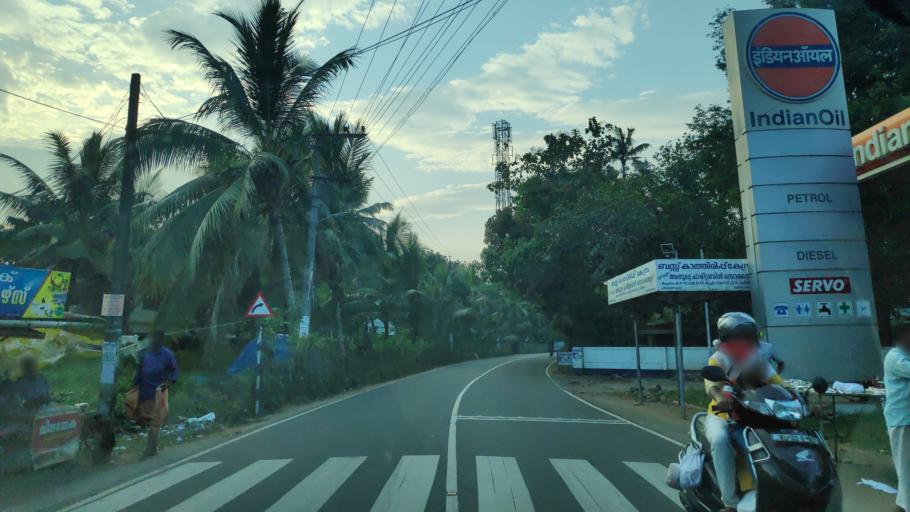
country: IN
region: Kerala
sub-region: Alappuzha
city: Shertallai
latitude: 9.6803
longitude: 76.3723
